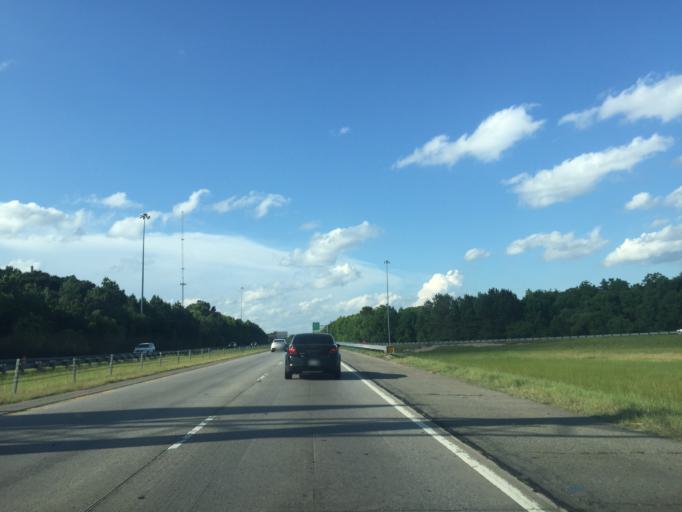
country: US
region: Georgia
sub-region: Chatham County
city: Savannah
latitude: 32.0446
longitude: -81.1461
